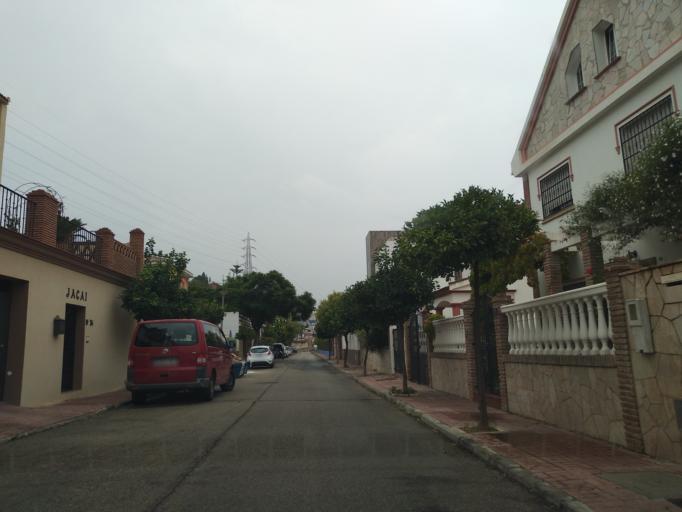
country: ES
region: Andalusia
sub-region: Provincia de Malaga
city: Malaga
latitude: 36.7417
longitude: -4.4753
